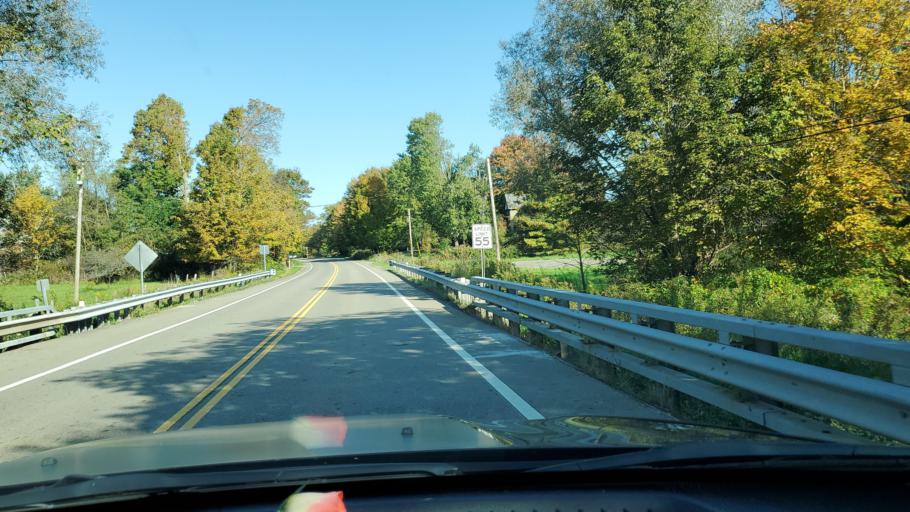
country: US
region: Ohio
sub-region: Trumbull County
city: Brookfield Center
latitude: 41.3935
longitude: -80.5687
